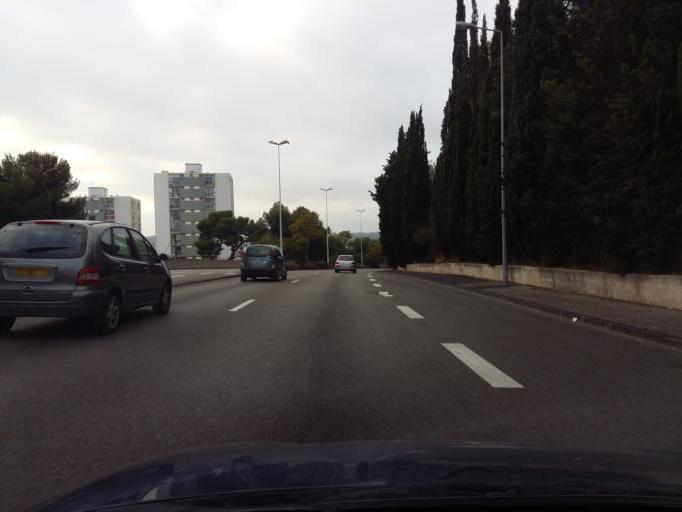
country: FR
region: Provence-Alpes-Cote d'Azur
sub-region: Departement des Bouches-du-Rhone
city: Martigues
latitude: 43.4159
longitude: 5.0565
